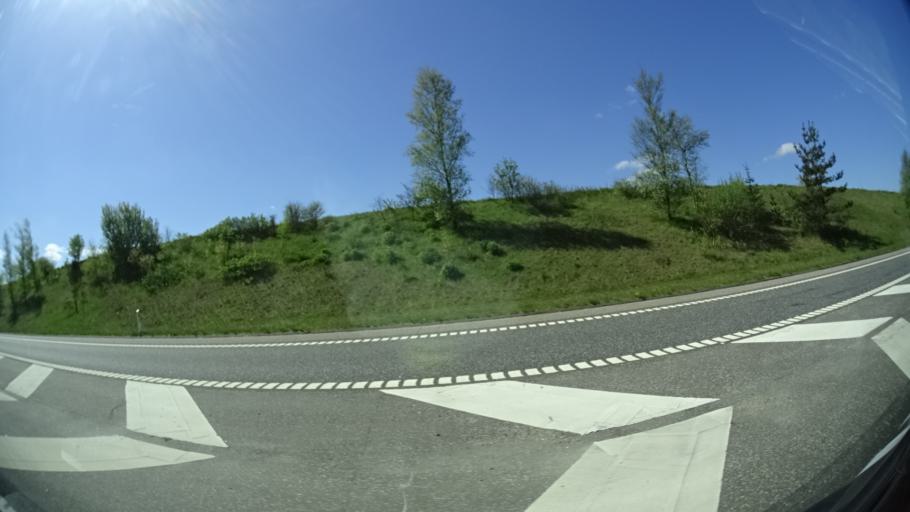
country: DK
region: Central Jutland
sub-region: Arhus Kommune
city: Trige
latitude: 56.3148
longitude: 10.1188
